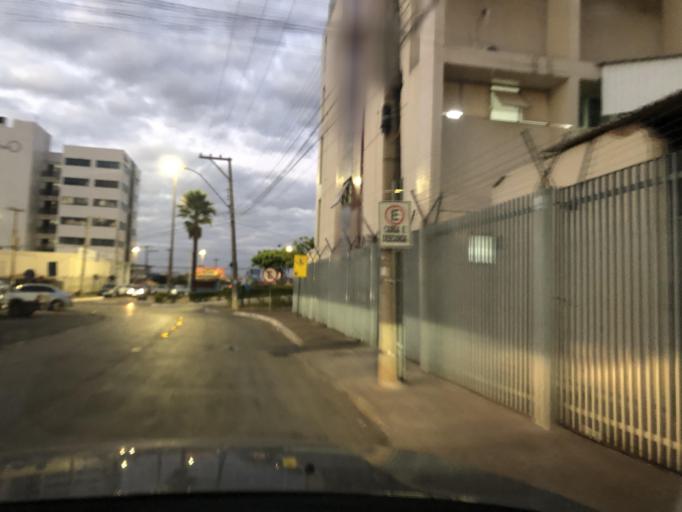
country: BR
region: Federal District
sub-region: Brasilia
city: Brasilia
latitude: -15.8532
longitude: -48.0735
